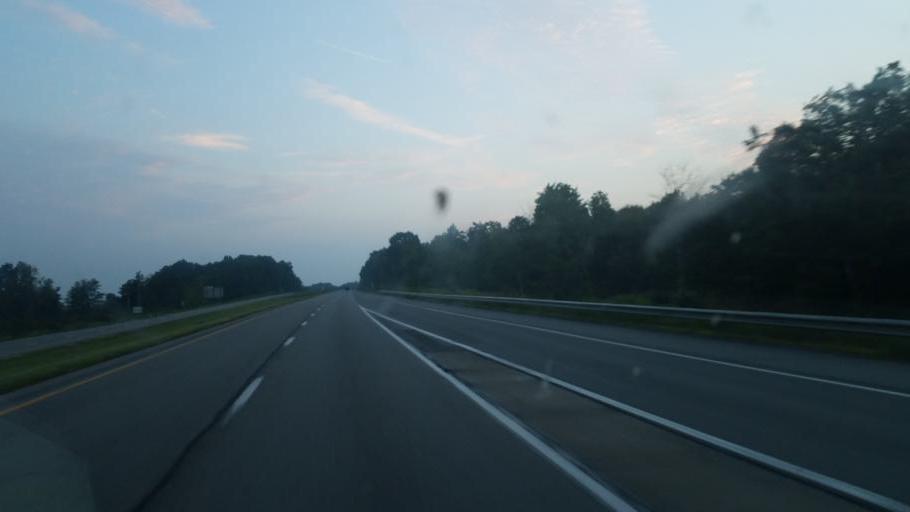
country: US
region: Pennsylvania
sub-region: Mercer County
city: Stoneboro
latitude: 41.3882
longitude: -80.1586
